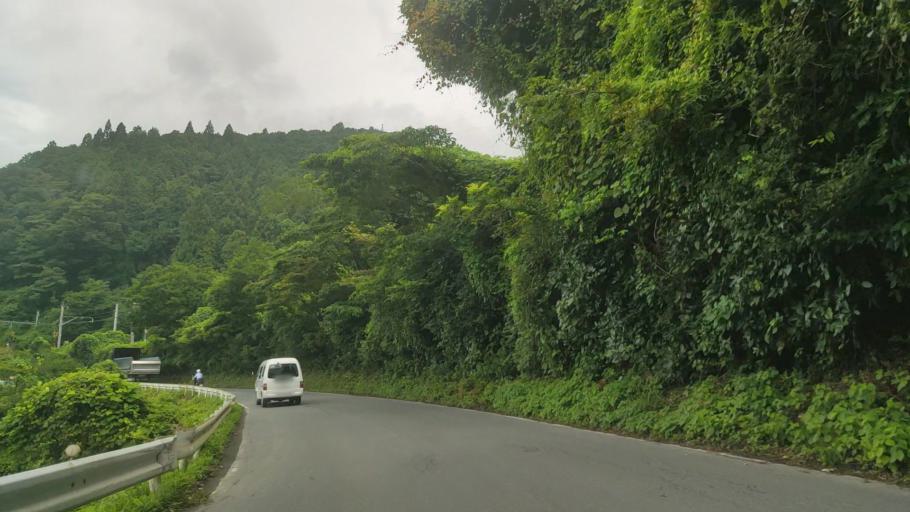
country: JP
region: Shizuoka
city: Fujinomiya
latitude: 35.2260
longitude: 138.5405
